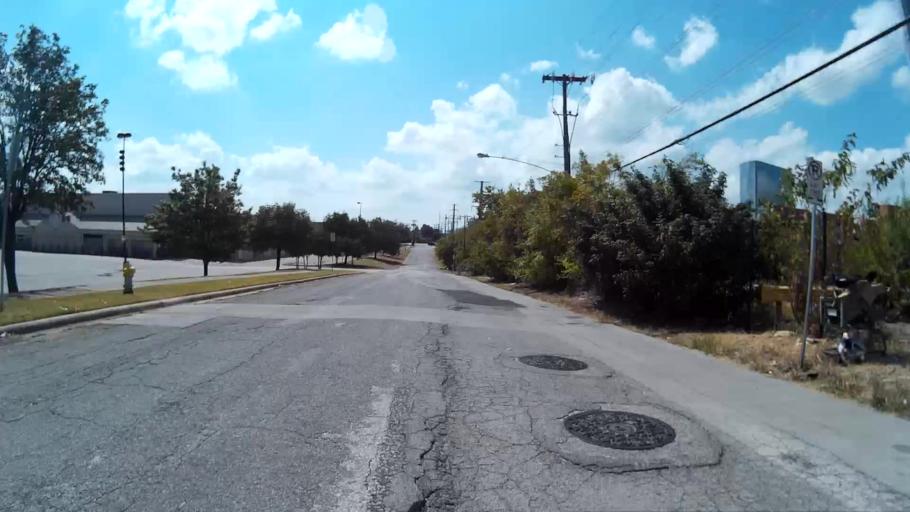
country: US
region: Texas
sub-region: Dallas County
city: University Park
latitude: 32.8698
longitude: -96.7651
